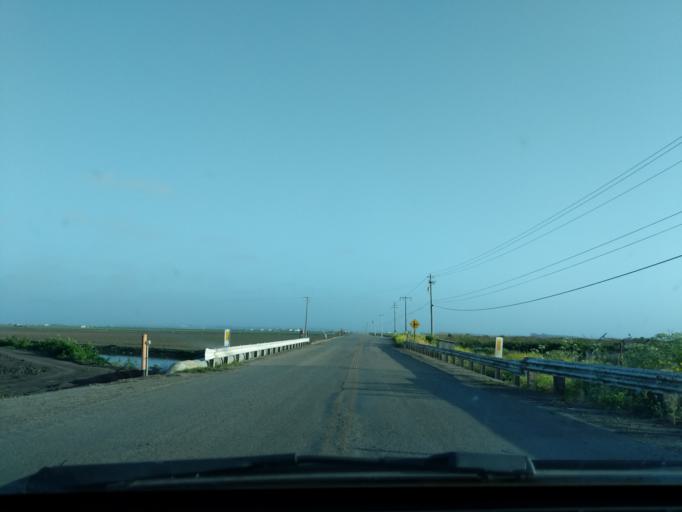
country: US
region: California
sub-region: Monterey County
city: Castroville
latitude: 36.7726
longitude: -121.7877
